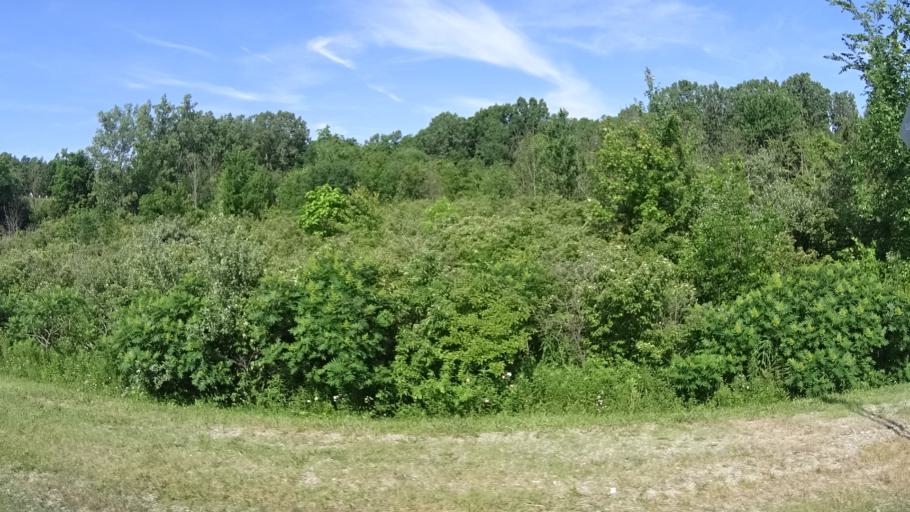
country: US
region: Ohio
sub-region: Erie County
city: Huron
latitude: 41.3687
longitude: -82.4581
